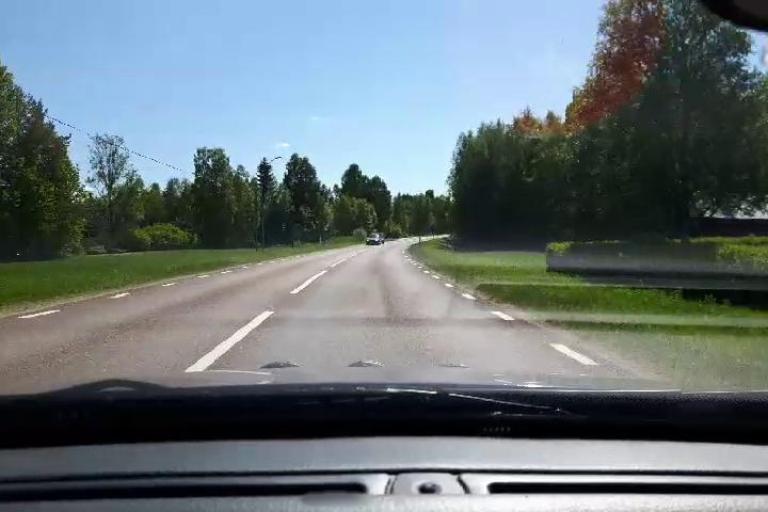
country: SE
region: Jaemtland
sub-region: Harjedalens Kommun
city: Sveg
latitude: 62.1565
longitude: 14.9537
